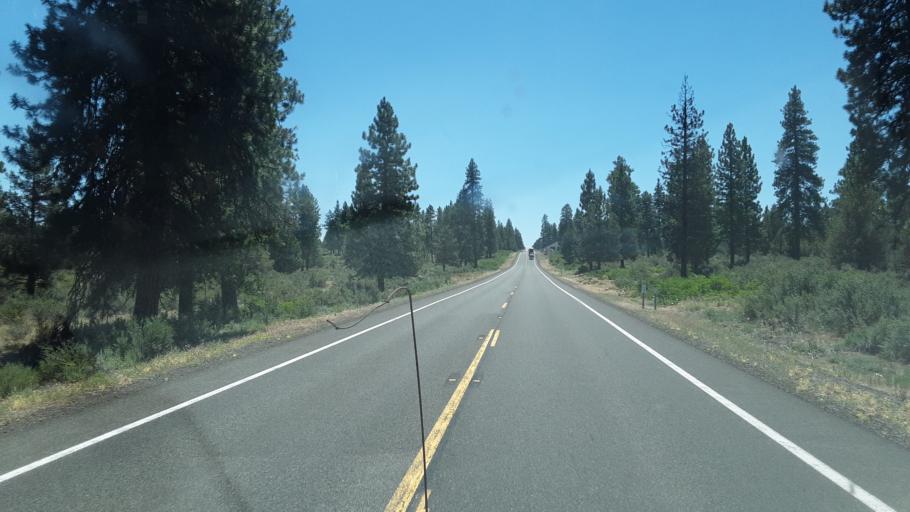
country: US
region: California
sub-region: Siskiyou County
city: Tulelake
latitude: 41.6159
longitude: -121.2159
